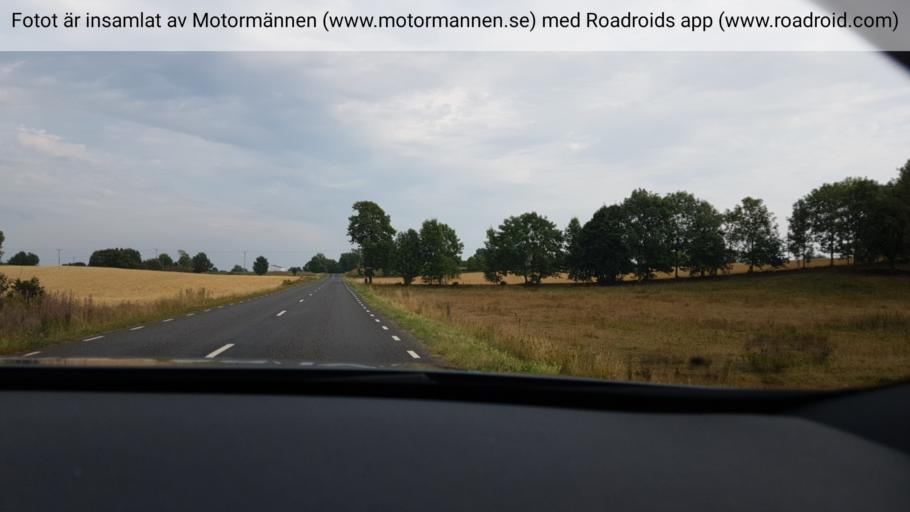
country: SE
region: Vaestra Goetaland
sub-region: Falkopings Kommun
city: Akarp
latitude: 58.1937
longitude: 13.6193
